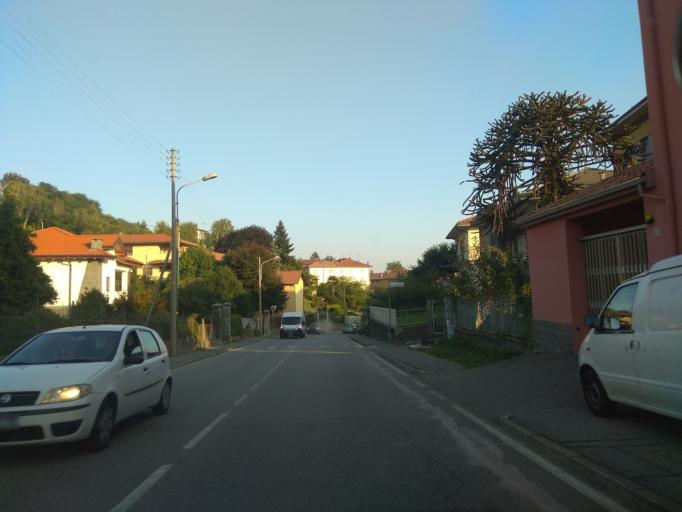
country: IT
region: Piedmont
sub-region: Provincia di Novara
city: Romagnano Sesia
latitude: 45.6366
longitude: 8.3854
